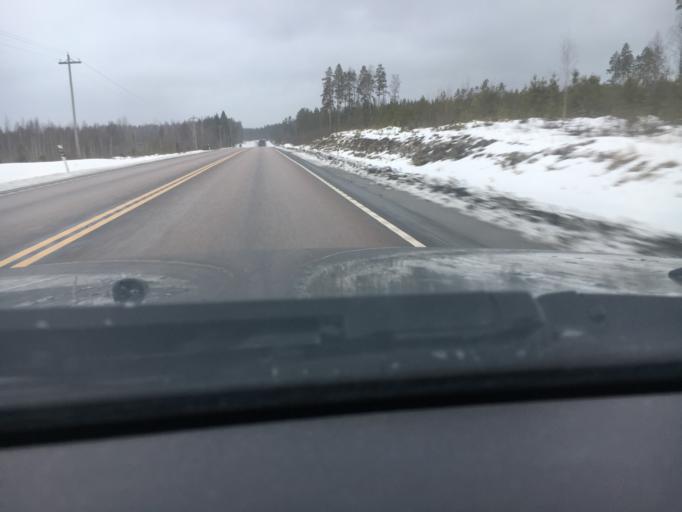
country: FI
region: Central Finland
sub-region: Joutsa
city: Leivonmaeki
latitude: 61.9583
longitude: 26.0972
